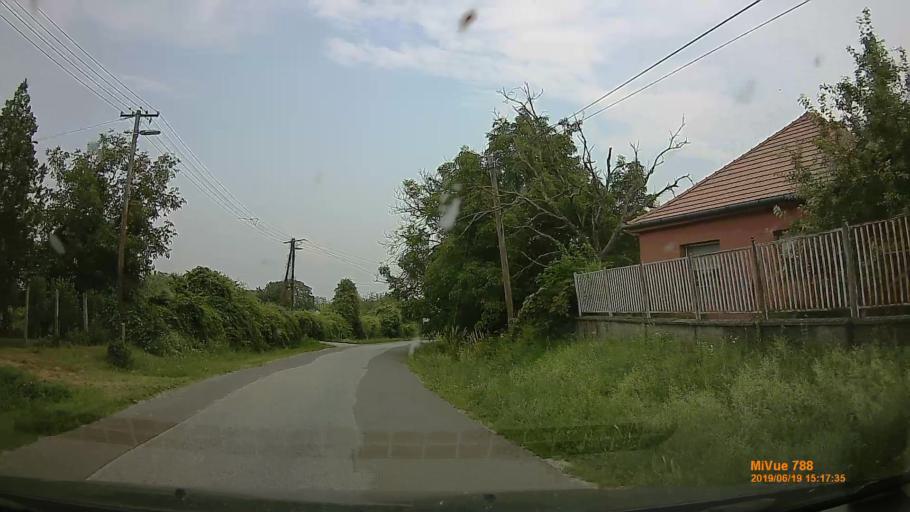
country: HU
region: Baranya
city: Szigetvar
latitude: 46.0797
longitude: 17.8485
